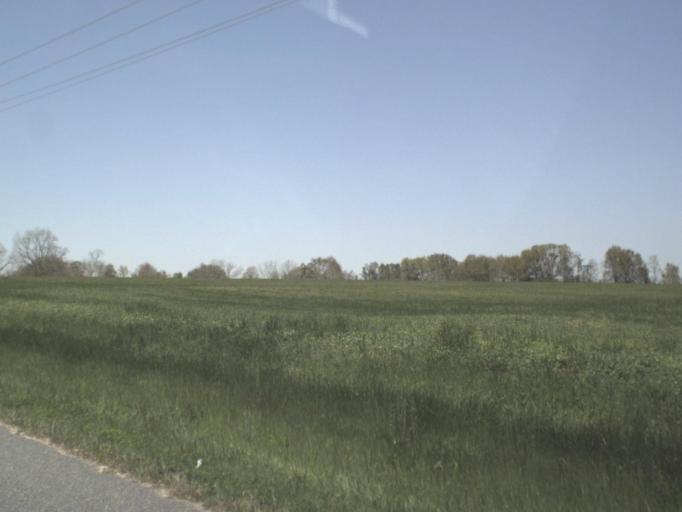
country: US
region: Florida
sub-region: Jackson County
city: Graceville
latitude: 30.9636
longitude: -85.5489
